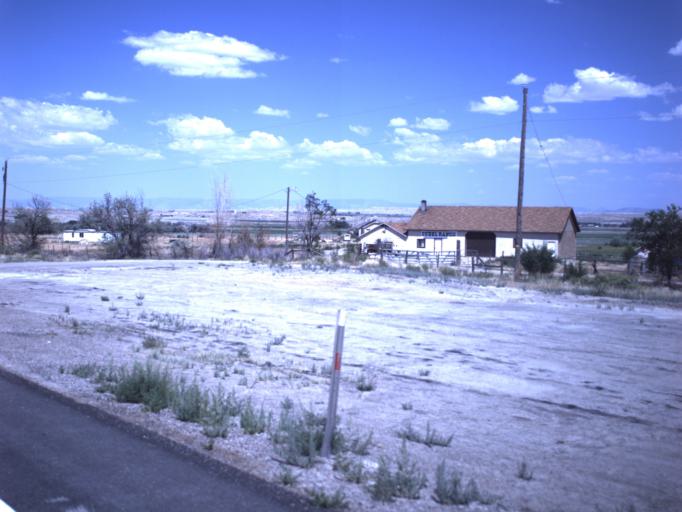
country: US
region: Utah
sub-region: Emery County
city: Huntington
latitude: 39.2860
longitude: -110.9725
